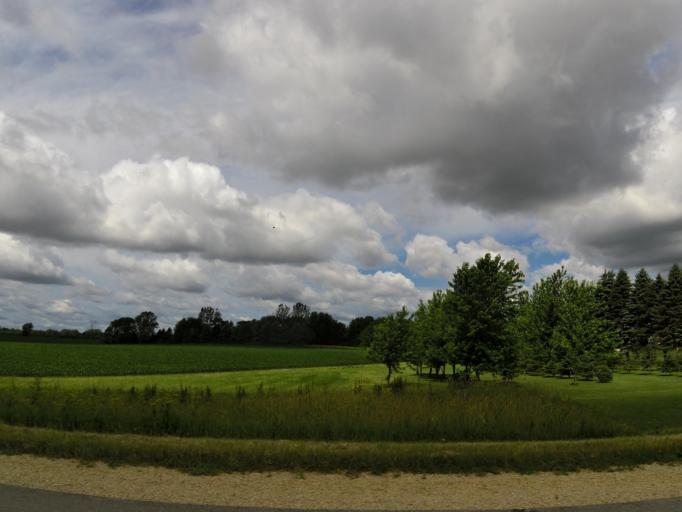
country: US
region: Minnesota
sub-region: Olmsted County
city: Stewartville
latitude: 43.8188
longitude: -92.4892
